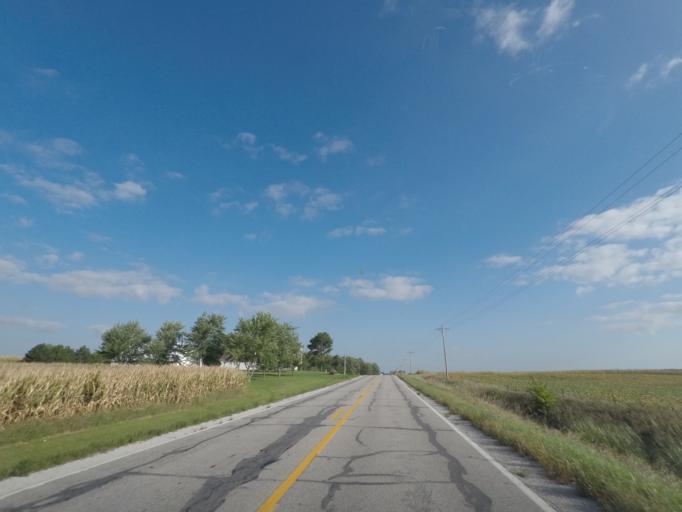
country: US
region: Iowa
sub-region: Story County
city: Nevada
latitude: 41.9855
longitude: -93.4629
